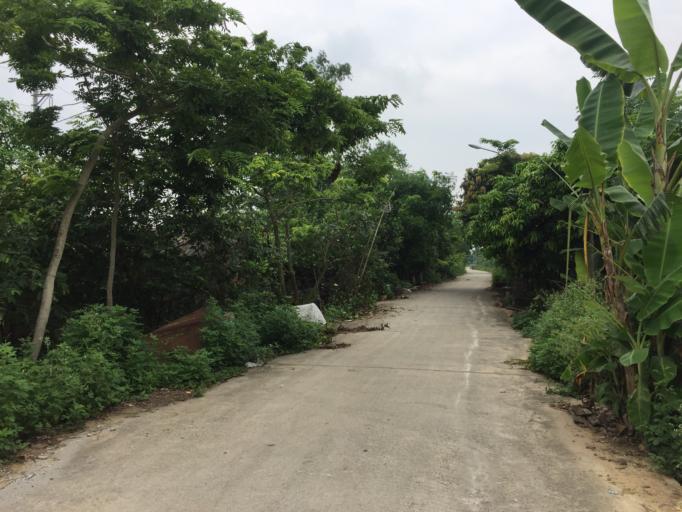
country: VN
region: Bac Ninh
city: Cho
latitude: 21.1251
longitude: 105.9344
